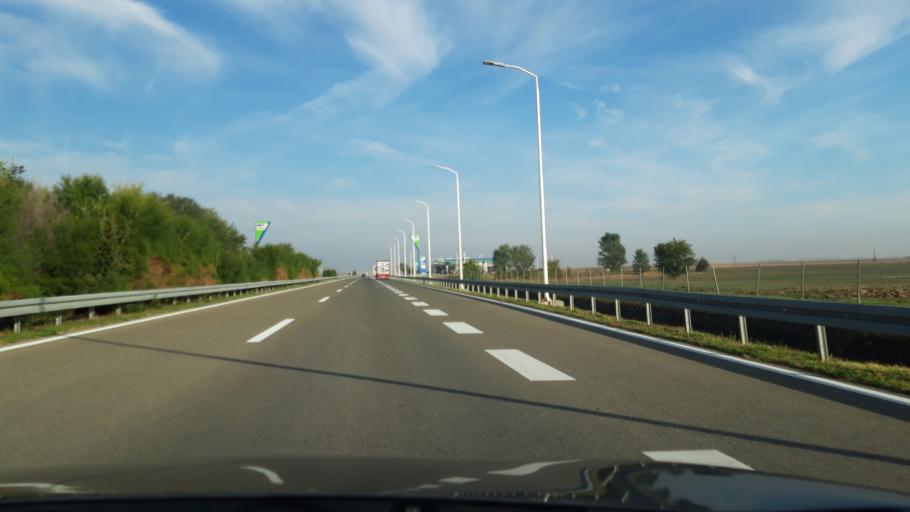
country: RS
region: Autonomna Pokrajina Vojvodina
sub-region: Severnobacki Okrug
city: Backa Topola
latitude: 45.7920
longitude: 19.6946
